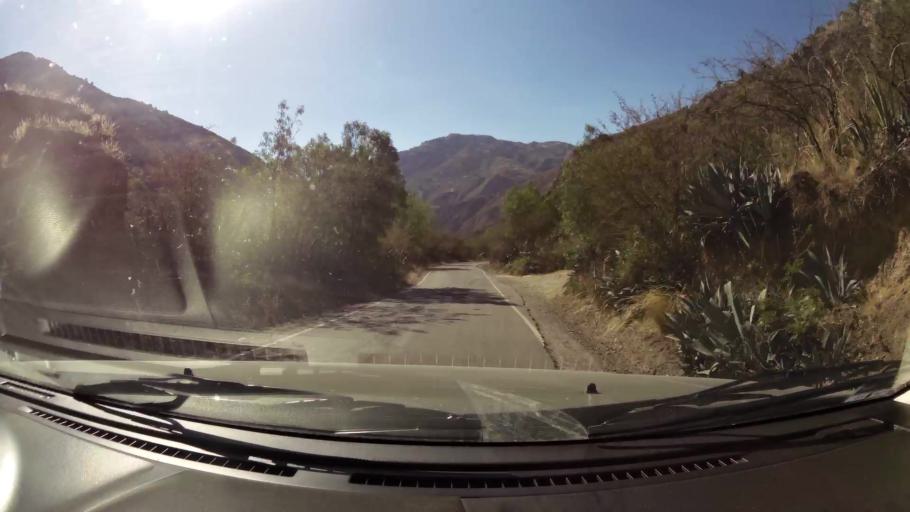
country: PE
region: Huancavelica
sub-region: Provincia de Acobamba
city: Pomacocha
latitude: -12.7816
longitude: -74.4976
